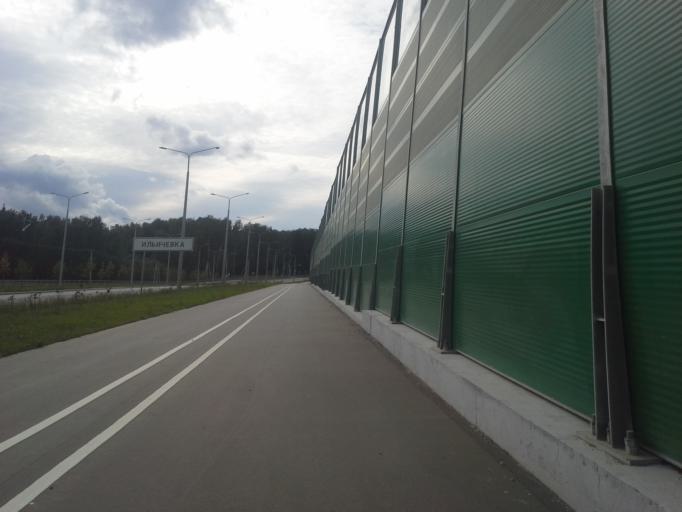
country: RU
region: Moskovskaya
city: Troitsk
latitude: 55.5031
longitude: 37.2725
